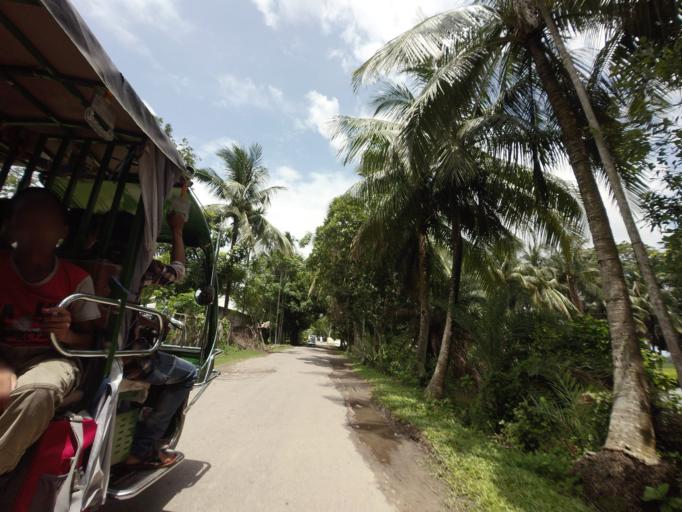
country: BD
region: Khulna
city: Kalia
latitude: 23.0402
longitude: 89.6376
